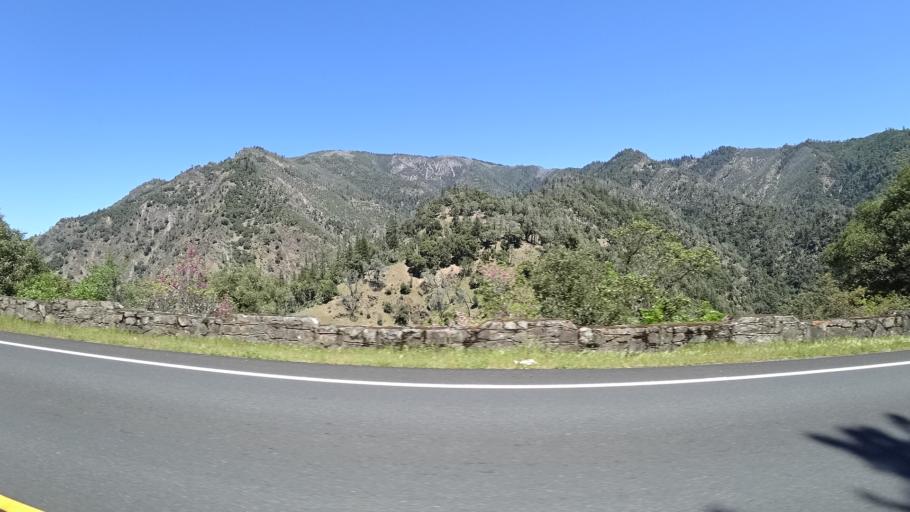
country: US
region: California
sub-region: Humboldt County
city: Willow Creek
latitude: 40.8039
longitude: -123.4665
